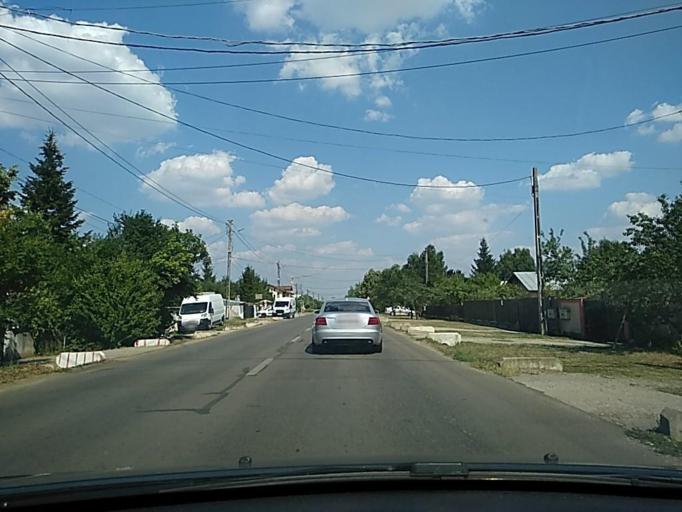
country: RO
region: Ilfov
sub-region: Comuna Clinceni
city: Olteni
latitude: 44.4033
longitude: 25.9438
